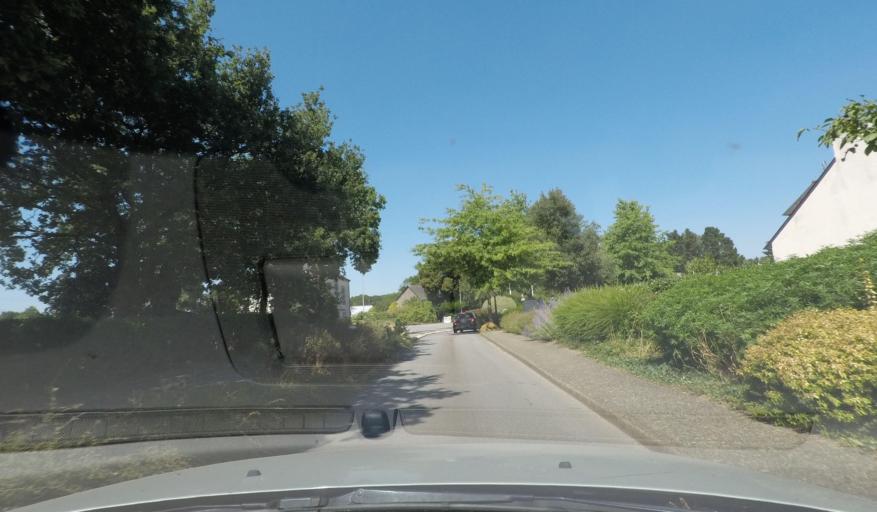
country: FR
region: Brittany
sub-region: Departement du Morbihan
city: Malestroit
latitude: 47.8127
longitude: -2.3728
